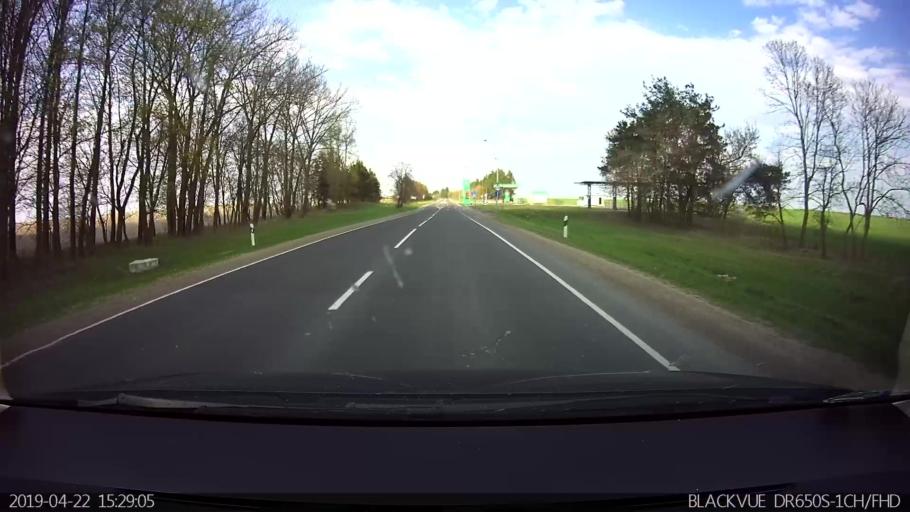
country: BY
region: Brest
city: Vysokaye
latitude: 52.3811
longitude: 23.3706
